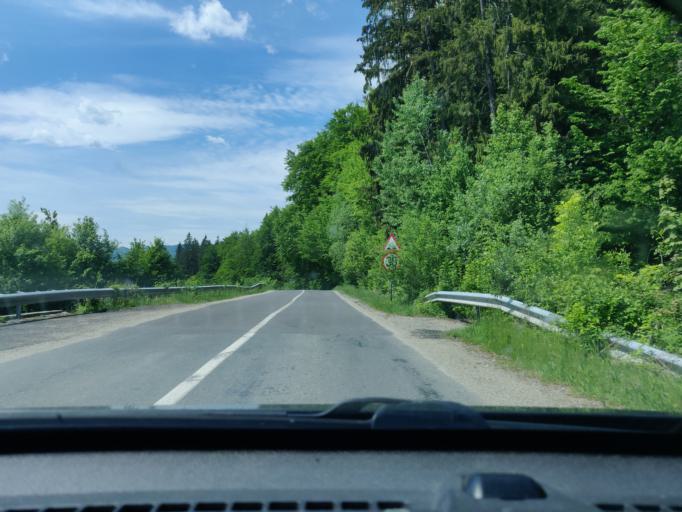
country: RO
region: Vrancea
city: Dragosloveni
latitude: 46.0360
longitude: 26.6988
